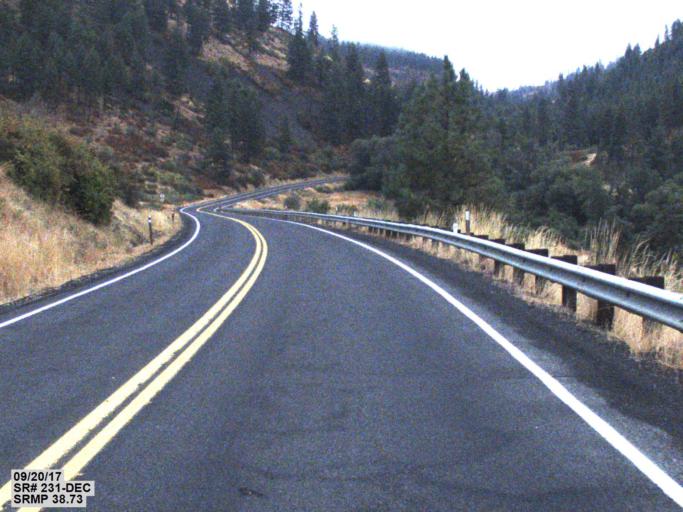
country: US
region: Washington
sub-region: Lincoln County
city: Davenport
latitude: 47.7720
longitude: -117.8933
